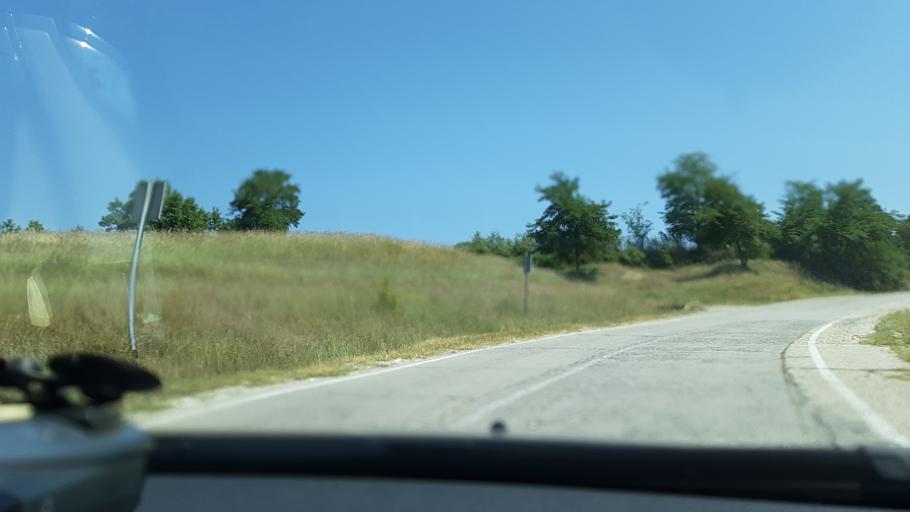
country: RO
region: Gorj
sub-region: Comuna Bustuchin
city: Bustuchin
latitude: 44.9152
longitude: 23.7669
